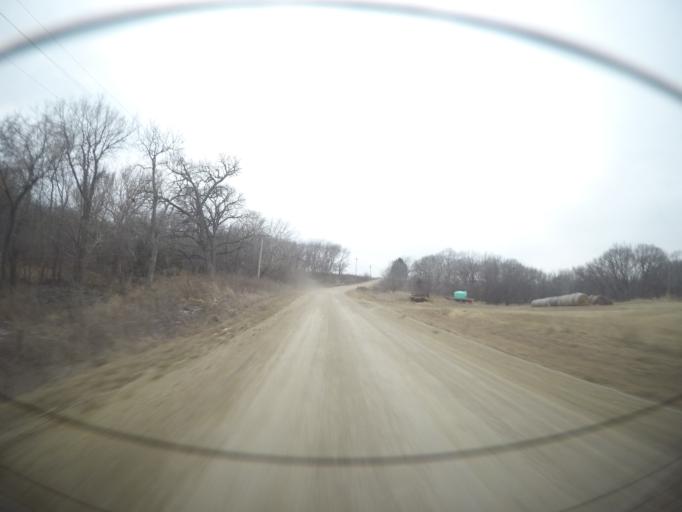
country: US
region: Kansas
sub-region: Pottawatomie County
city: Wamego
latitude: 39.1524
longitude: -96.2883
